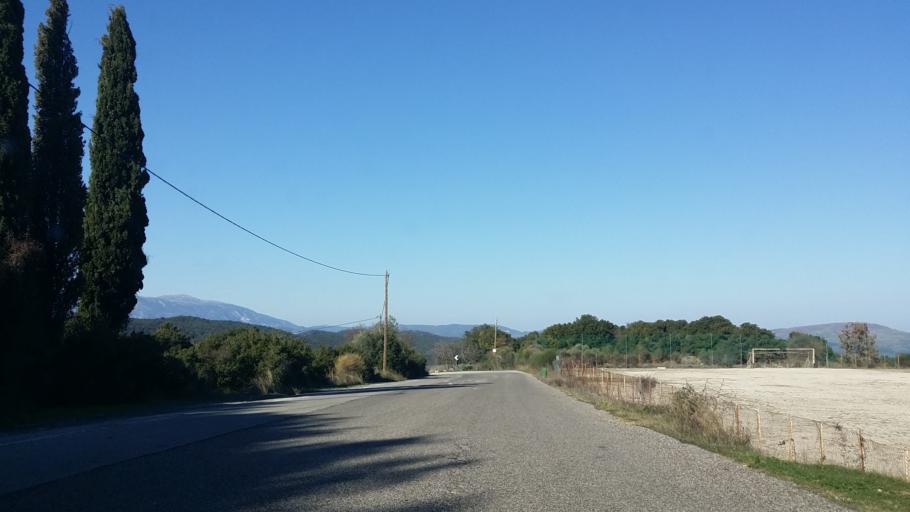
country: GR
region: West Greece
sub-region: Nomos Aitolias kai Akarnanias
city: Fitiai
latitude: 38.7065
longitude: 21.1830
